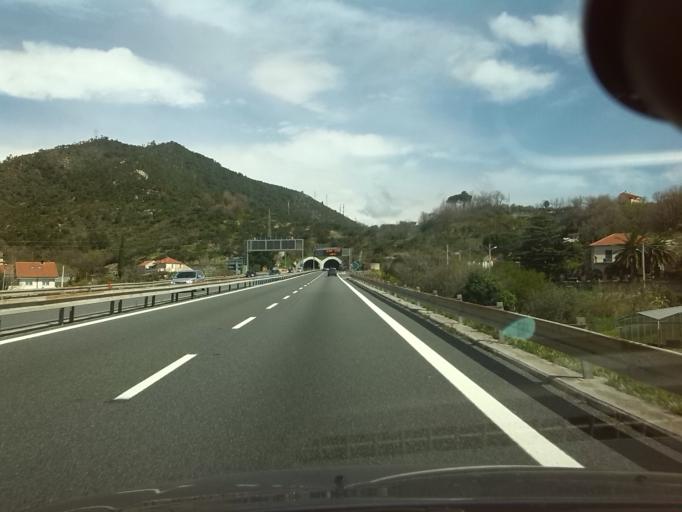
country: IT
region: Liguria
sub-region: Provincia di Savona
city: Loano
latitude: 44.1395
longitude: 8.2441
